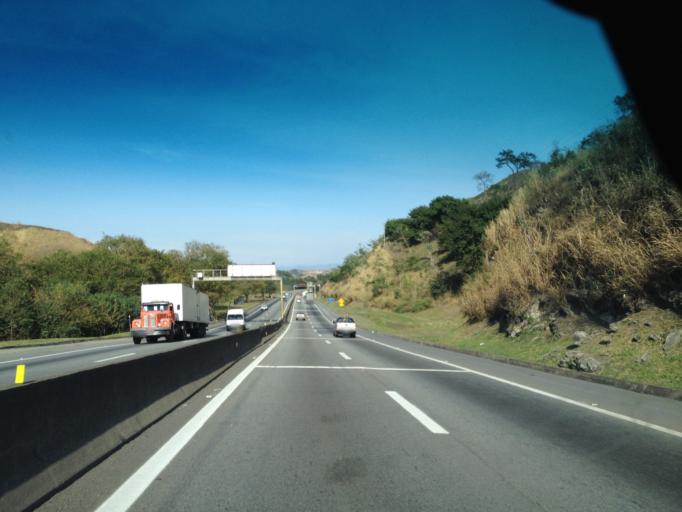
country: BR
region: Rio de Janeiro
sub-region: Barra Mansa
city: Barra Mansa
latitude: -22.5569
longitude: -44.1322
